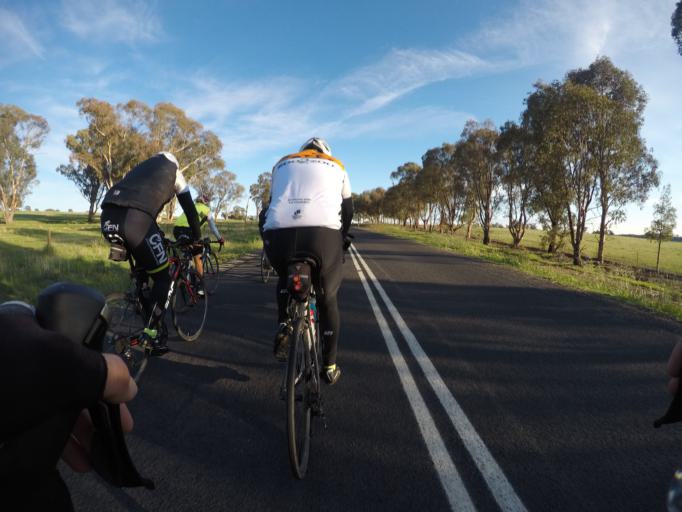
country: AU
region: New South Wales
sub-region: Cabonne
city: Molong
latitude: -33.0341
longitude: 148.8082
